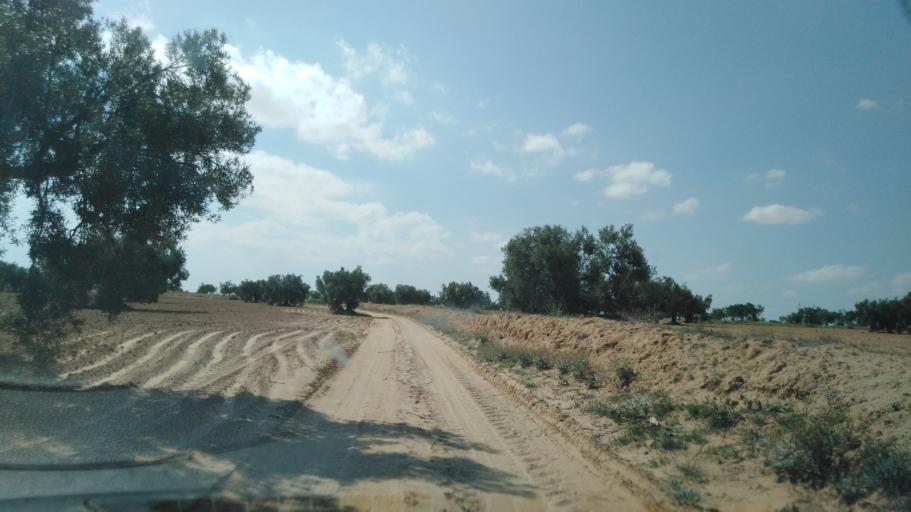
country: TN
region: Safaqis
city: Bi'r `Ali Bin Khalifah
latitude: 34.7941
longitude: 10.3961
